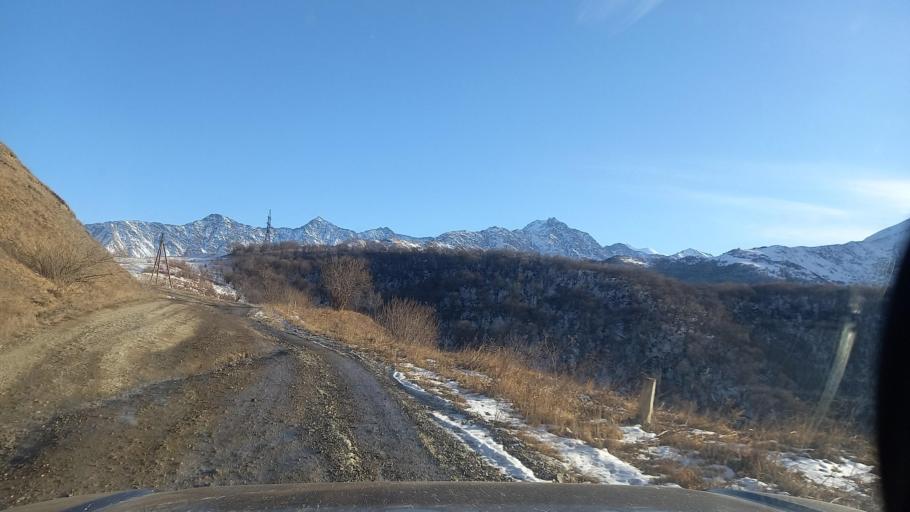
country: RU
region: North Ossetia
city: Verkhniy Fiagdon
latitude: 42.8358
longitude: 44.4748
